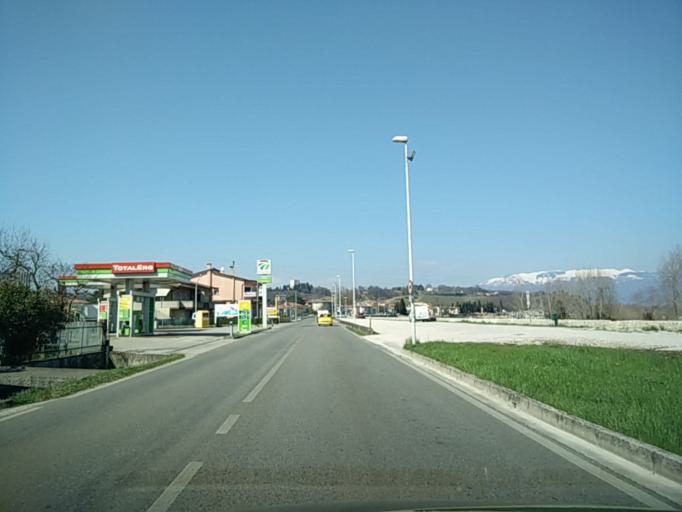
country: IT
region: Veneto
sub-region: Provincia di Treviso
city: Nervesa della Battaglia
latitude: 45.8237
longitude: 12.2179
